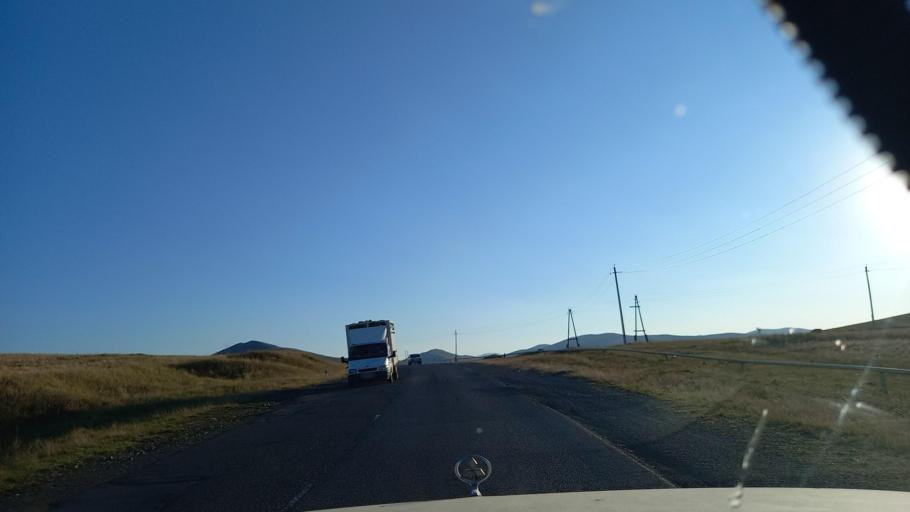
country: AZ
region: Shamkir Rayon
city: Shamkhor
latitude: 40.7582
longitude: 45.9073
